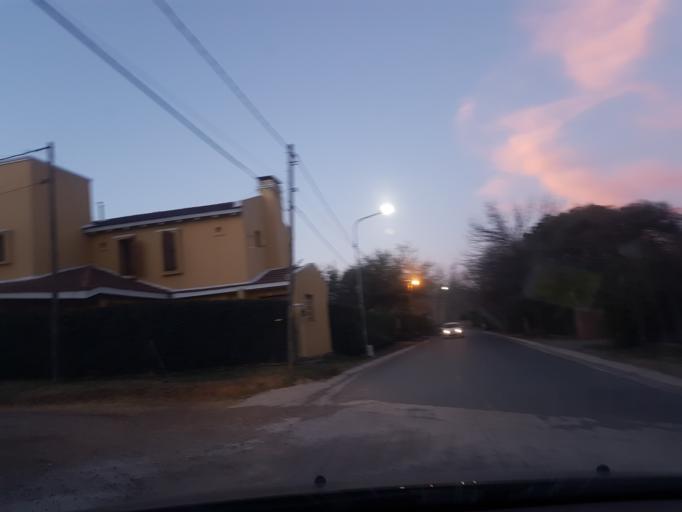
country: AR
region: Cordoba
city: Villa Allende
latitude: -31.2788
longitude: -64.2831
